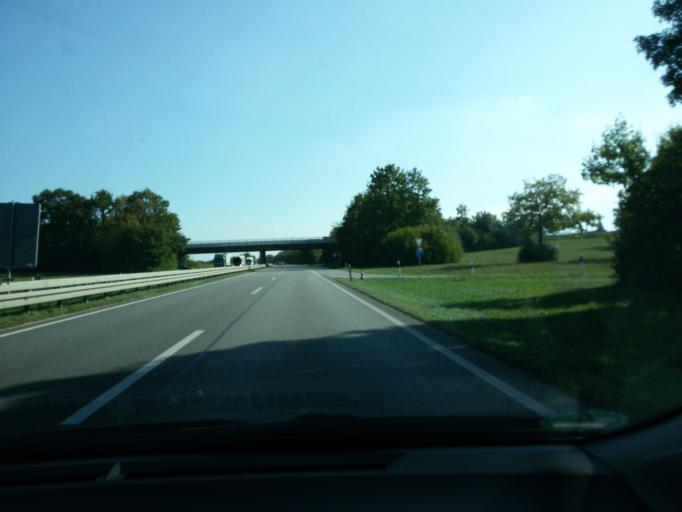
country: DE
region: Bavaria
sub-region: Swabia
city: Asbach-Baumenheim
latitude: 48.7039
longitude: 10.8058
